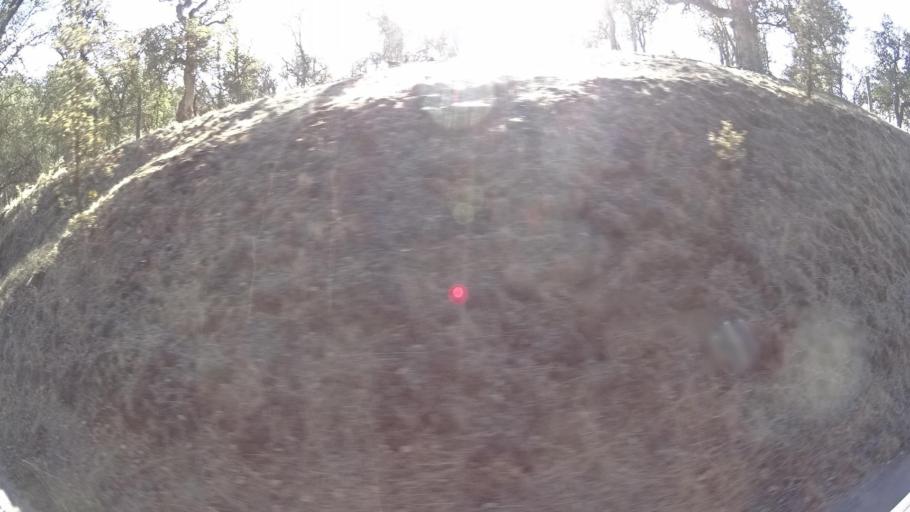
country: US
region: California
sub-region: Kern County
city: Alta Sierra
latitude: 35.6312
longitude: -118.7662
